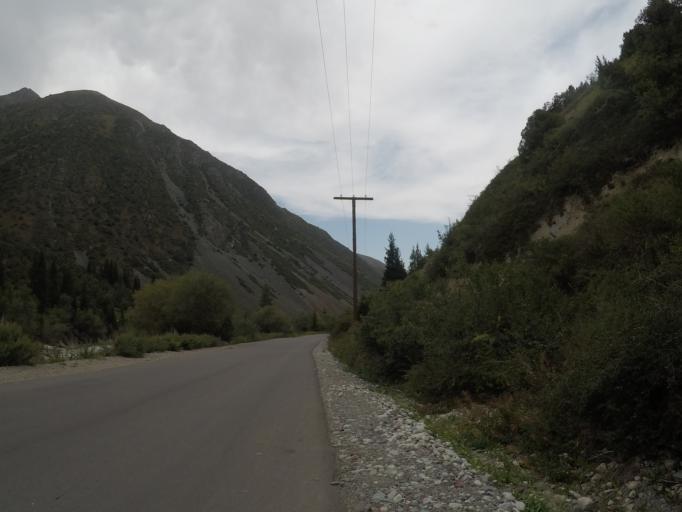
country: KG
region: Chuy
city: Bishkek
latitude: 42.5760
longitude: 74.4822
